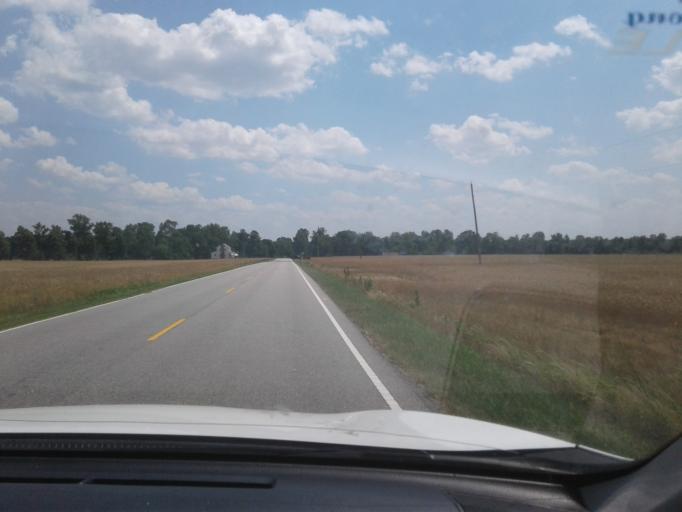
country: US
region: North Carolina
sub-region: Harnett County
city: Erwin
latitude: 35.2509
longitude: -78.6805
